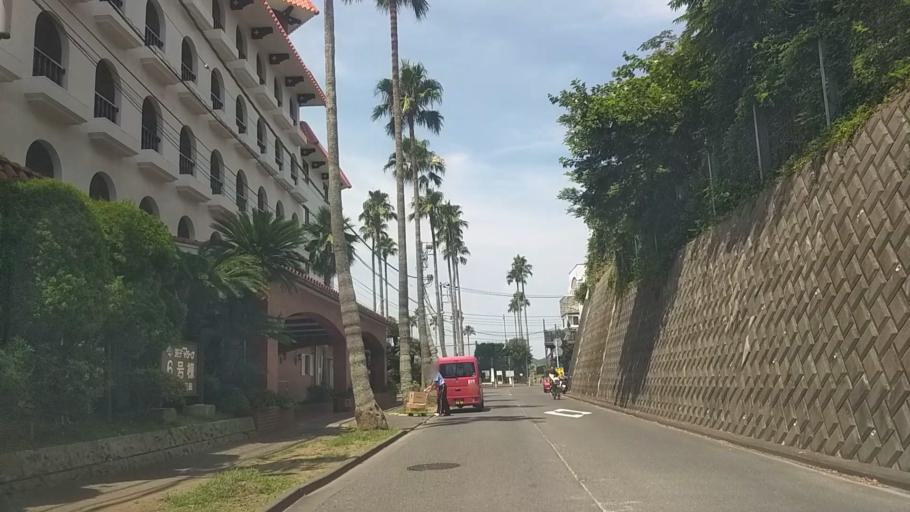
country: JP
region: Kanagawa
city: Kamakura
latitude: 35.2983
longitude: 139.5534
